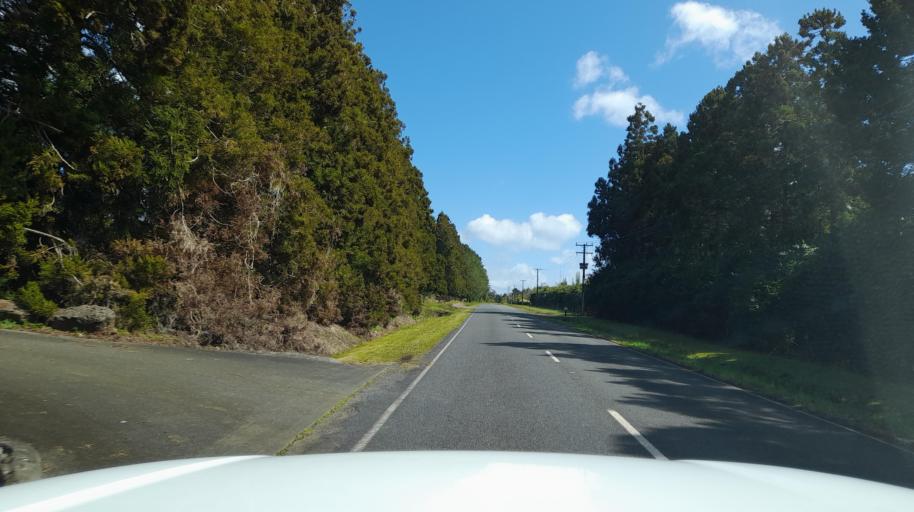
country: NZ
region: Northland
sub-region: Far North District
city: Kerikeri
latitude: -35.2408
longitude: 173.8917
